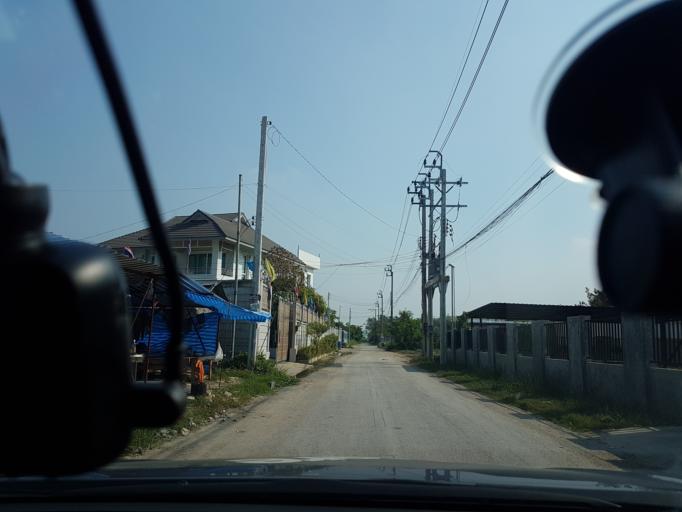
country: TH
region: Bangkok
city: Sai Mai
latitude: 13.9033
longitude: 100.6998
